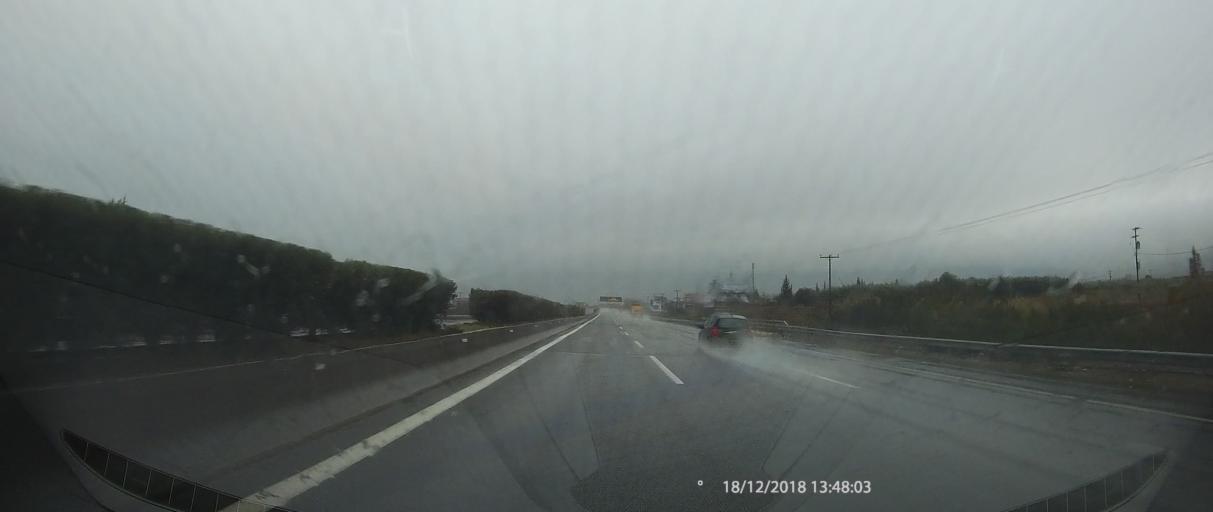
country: GR
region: Central Macedonia
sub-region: Nomos Pierias
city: Leptokarya
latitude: 40.0627
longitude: 22.5556
